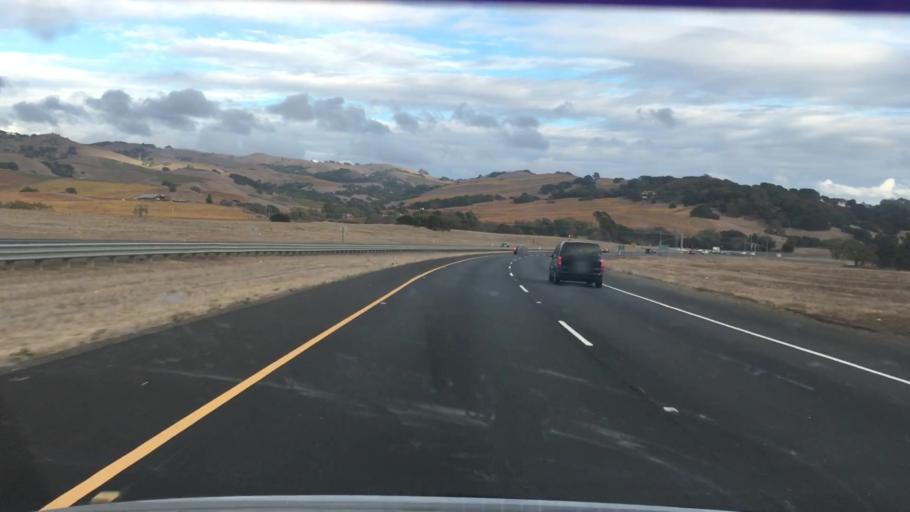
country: US
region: California
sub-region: Napa County
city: Napa
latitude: 38.2429
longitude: -122.2746
